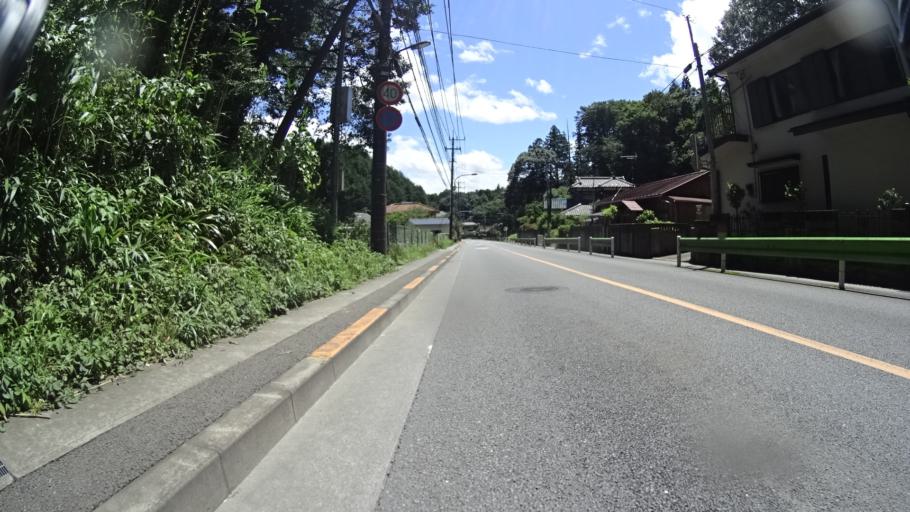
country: JP
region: Tokyo
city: Ome
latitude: 35.8016
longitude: 139.2653
